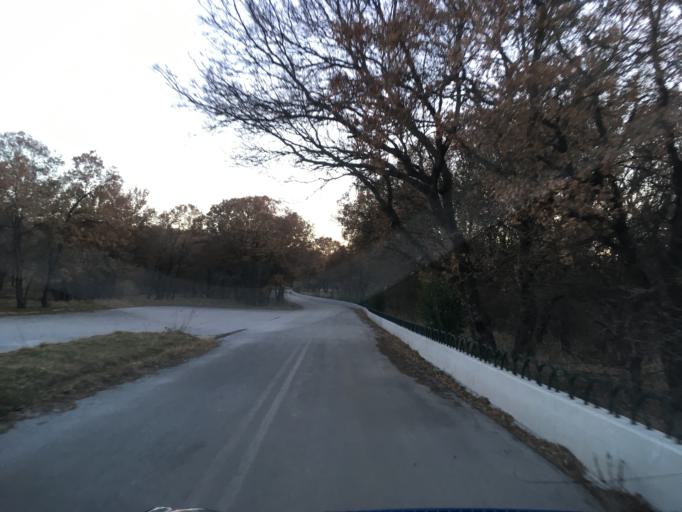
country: GR
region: West Macedonia
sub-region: Nomos Kozanis
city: Koila
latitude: 40.3289
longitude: 21.8319
